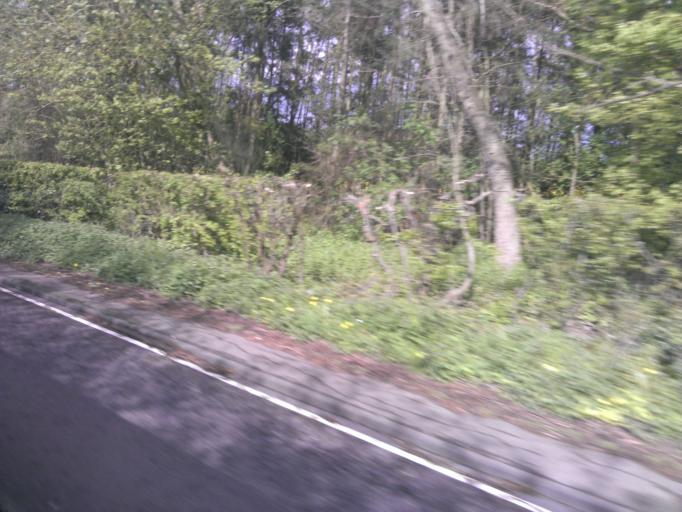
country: GB
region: England
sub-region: Essex
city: Eight Ash Green
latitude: 51.9048
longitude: 0.7927
